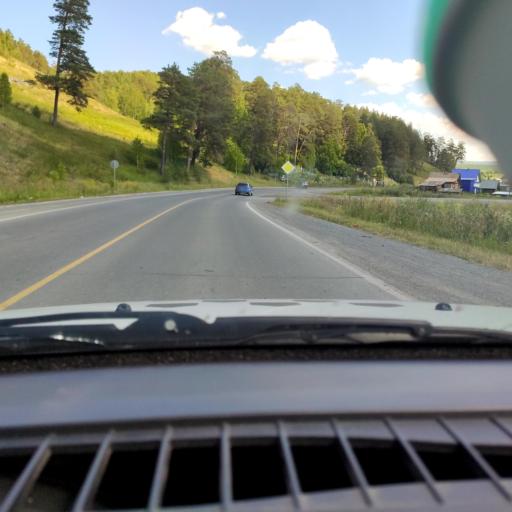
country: RU
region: Chelyabinsk
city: Mezhevoy
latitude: 55.1590
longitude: 58.8125
